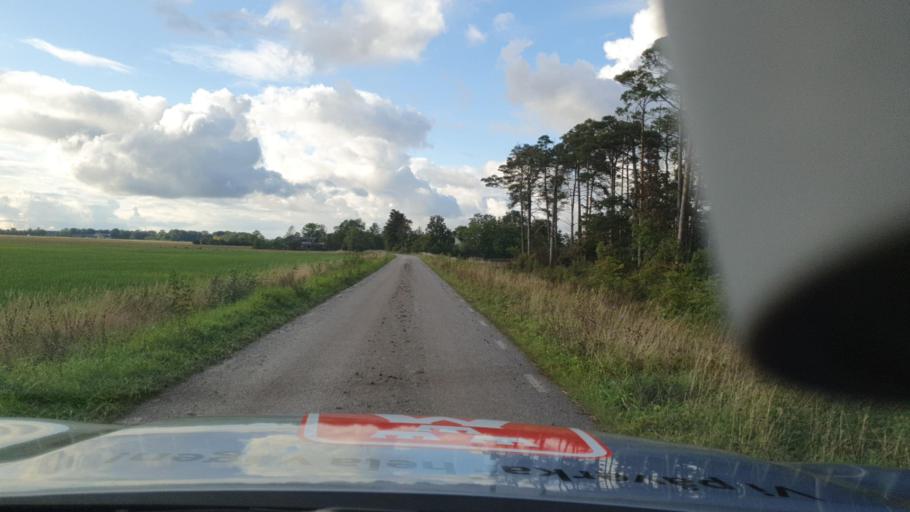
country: SE
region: Gotland
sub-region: Gotland
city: Hemse
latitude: 57.2094
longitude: 18.2362
